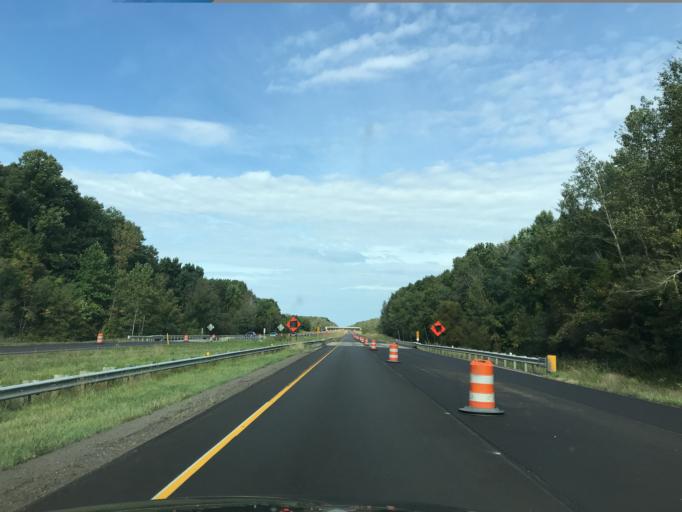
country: US
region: Ohio
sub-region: Ashtabula County
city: Jefferson
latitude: 41.7774
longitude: -80.7295
